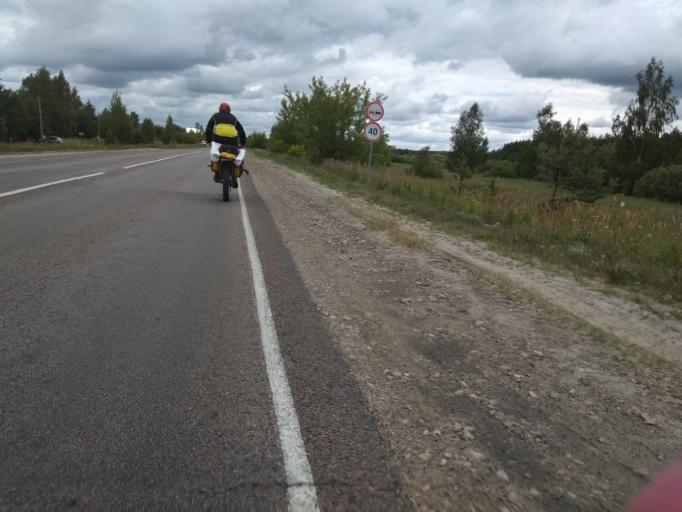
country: RU
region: Moskovskaya
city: Kerva
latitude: 55.5849
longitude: 39.6979
